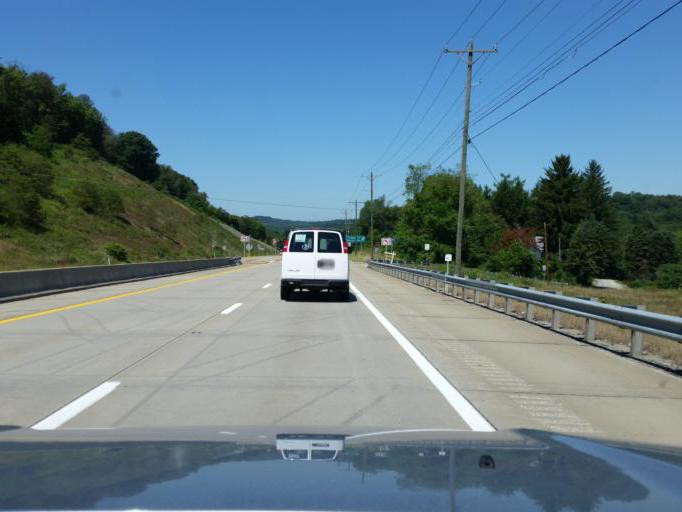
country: US
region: Pennsylvania
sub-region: Westmoreland County
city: Murrysville
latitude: 40.4160
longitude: -79.6431
